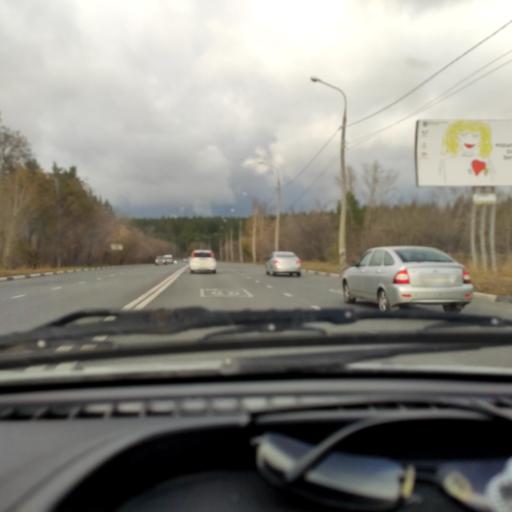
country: RU
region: Samara
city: Zhigulevsk
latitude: 53.4993
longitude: 49.4727
